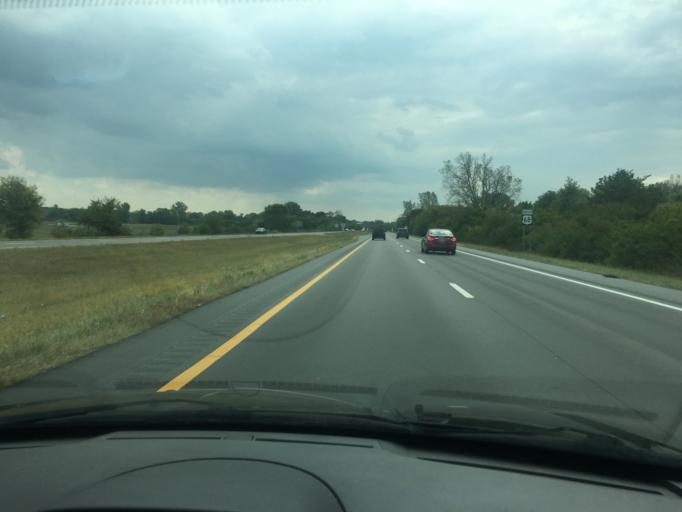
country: US
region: Ohio
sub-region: Clark County
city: Northridge
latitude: 39.9791
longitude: -83.8153
